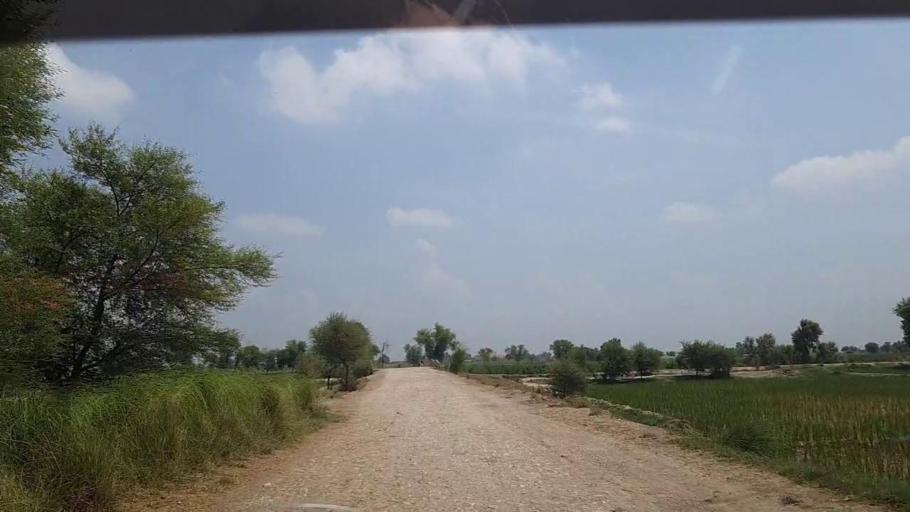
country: PK
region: Sindh
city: Khanpur
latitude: 27.8910
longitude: 69.4030
